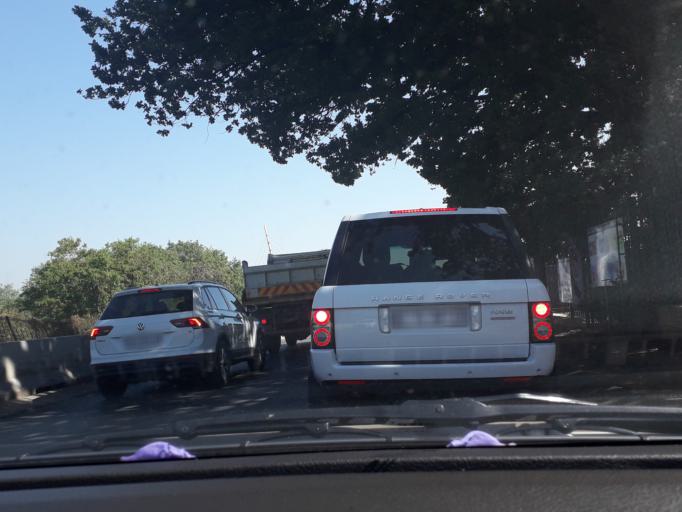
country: ZA
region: Gauteng
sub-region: City of Johannesburg Metropolitan Municipality
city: Modderfontein
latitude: -26.1110
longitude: 28.0780
